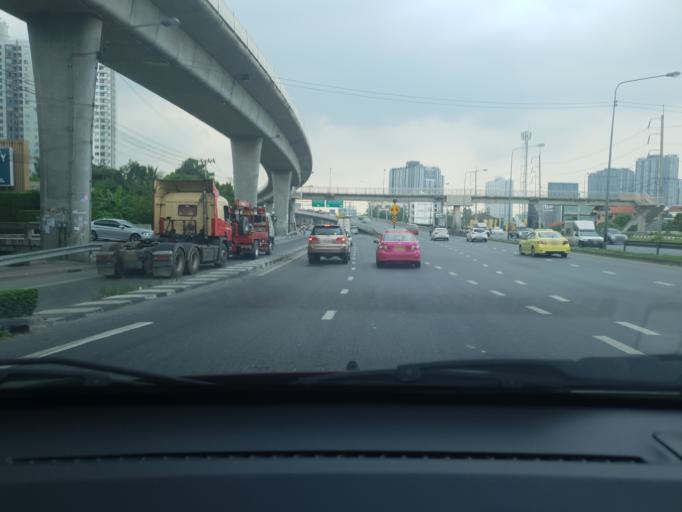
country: TH
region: Bangkok
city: Bangkok Yai
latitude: 13.7142
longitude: 100.4660
